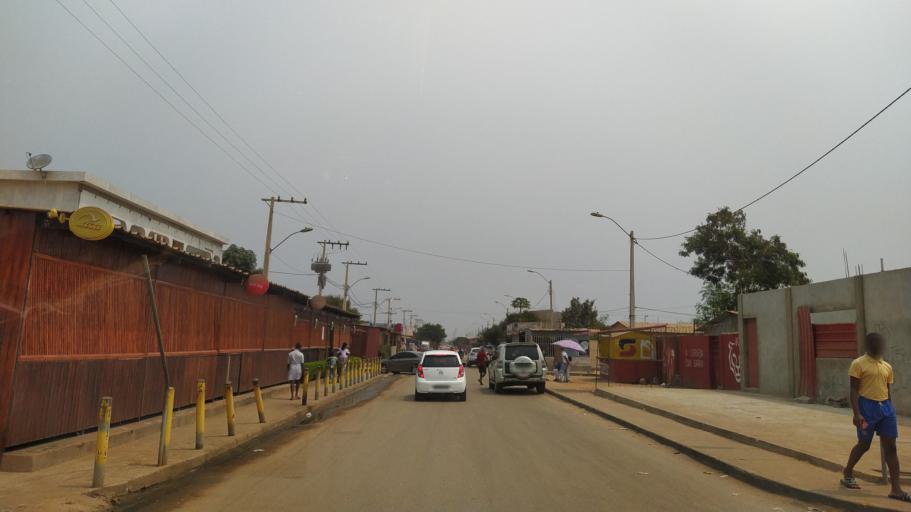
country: AO
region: Luanda
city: Luanda
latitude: -9.0726
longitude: 13.4061
